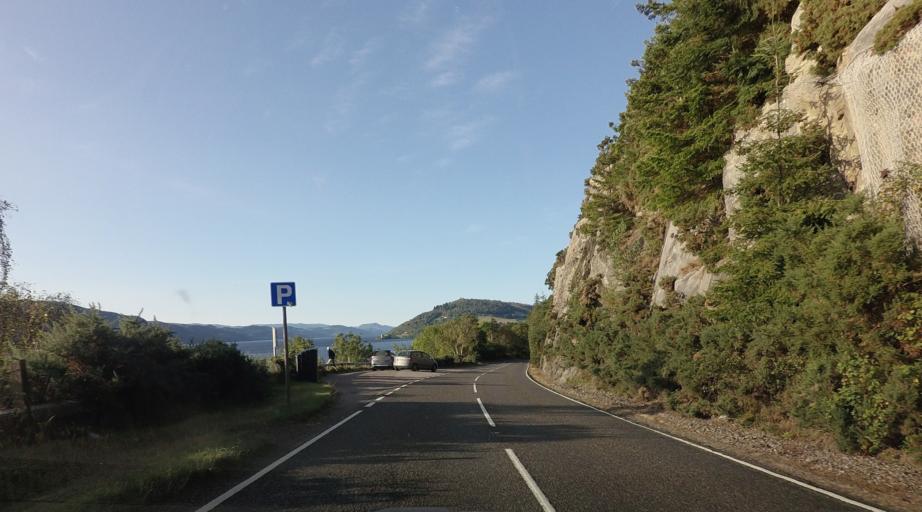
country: GB
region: Scotland
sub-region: Highland
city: Beauly
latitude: 57.3444
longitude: -4.4206
